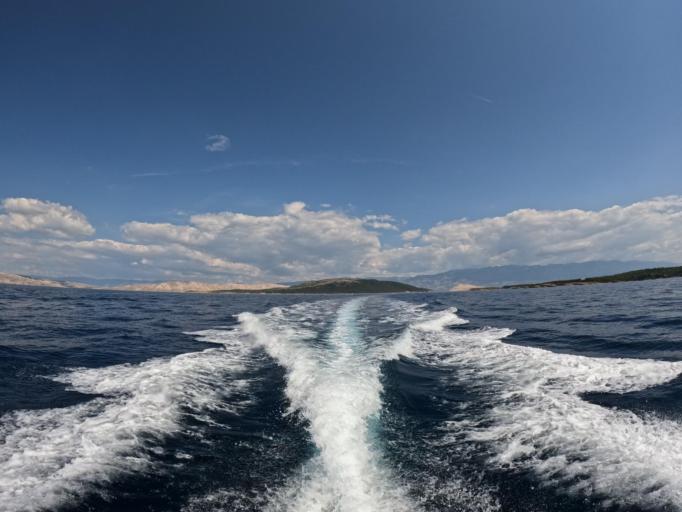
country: HR
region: Primorsko-Goranska
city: Lopar
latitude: 44.8561
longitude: 14.7081
